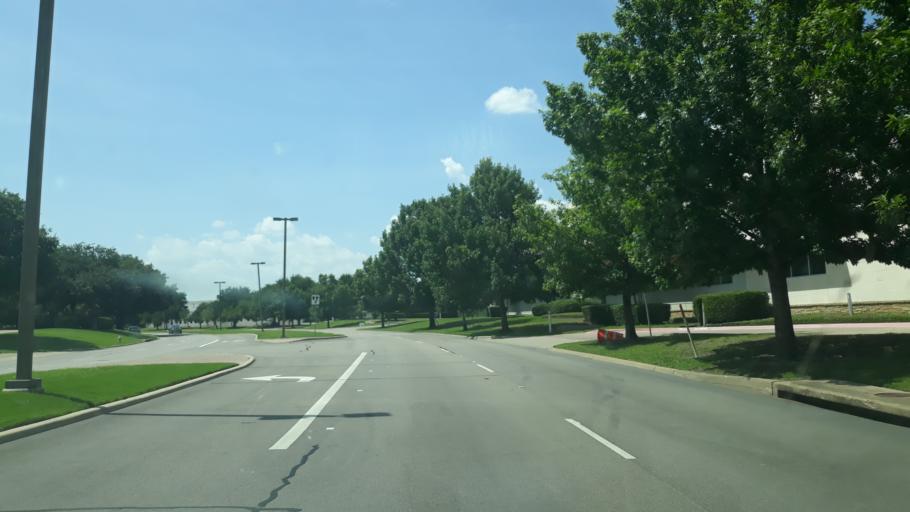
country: US
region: Texas
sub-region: Dallas County
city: Coppell
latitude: 32.9566
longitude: -97.0224
